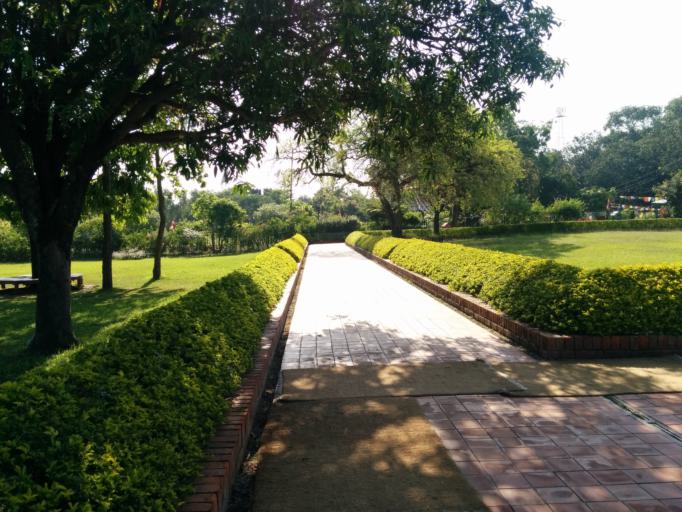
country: IN
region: Uttar Pradesh
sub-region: Maharajganj
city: Nautanwa
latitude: 27.4700
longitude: 83.2759
